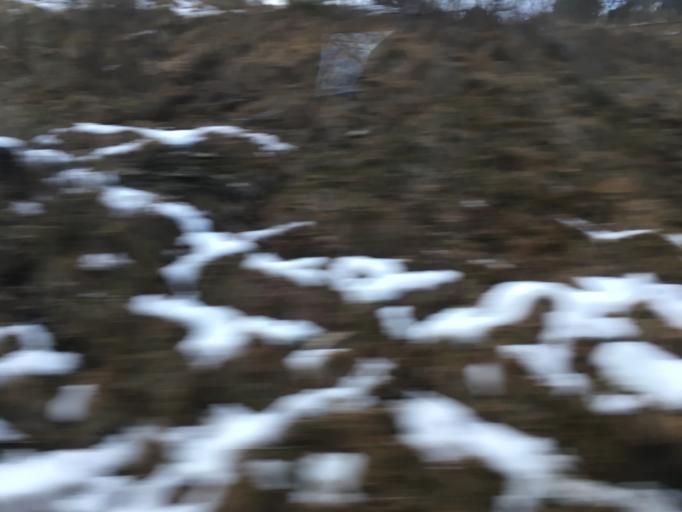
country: CH
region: Grisons
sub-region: Albula District
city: Tiefencastel
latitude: 46.6646
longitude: 9.5839
